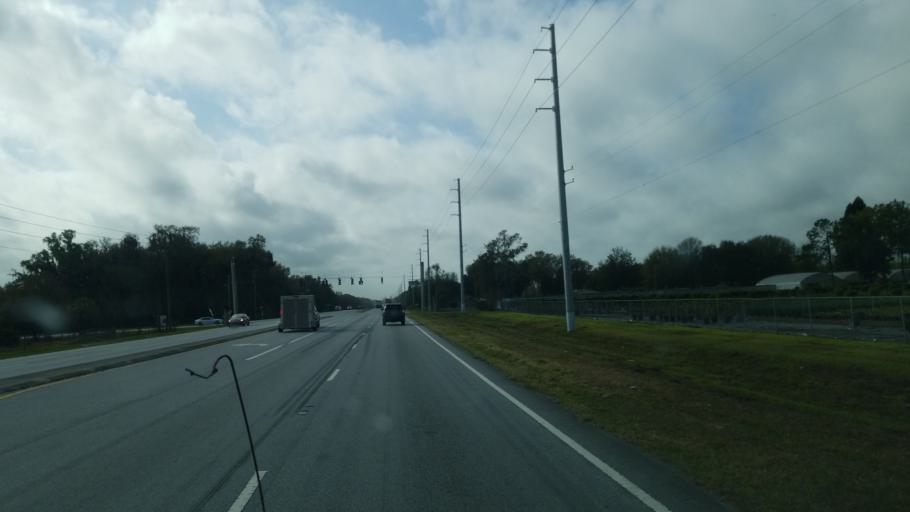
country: US
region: Florida
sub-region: Polk County
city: Willow Oak
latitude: 27.9721
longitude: -82.0557
